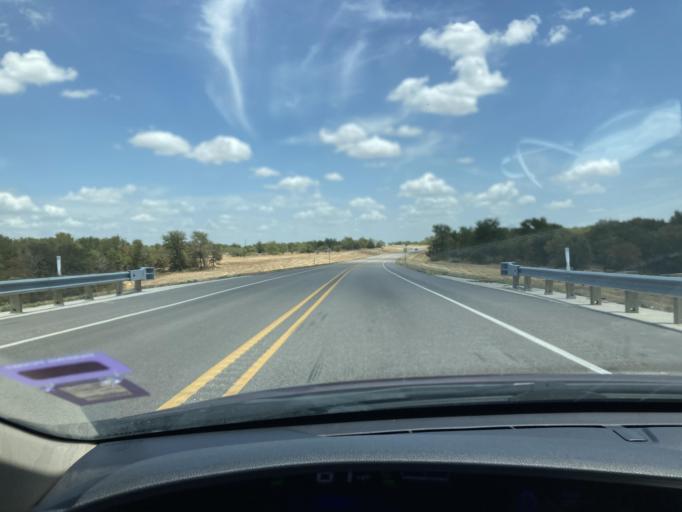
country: US
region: Texas
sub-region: Navarro County
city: Corsicana
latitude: 32.0569
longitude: -96.4107
